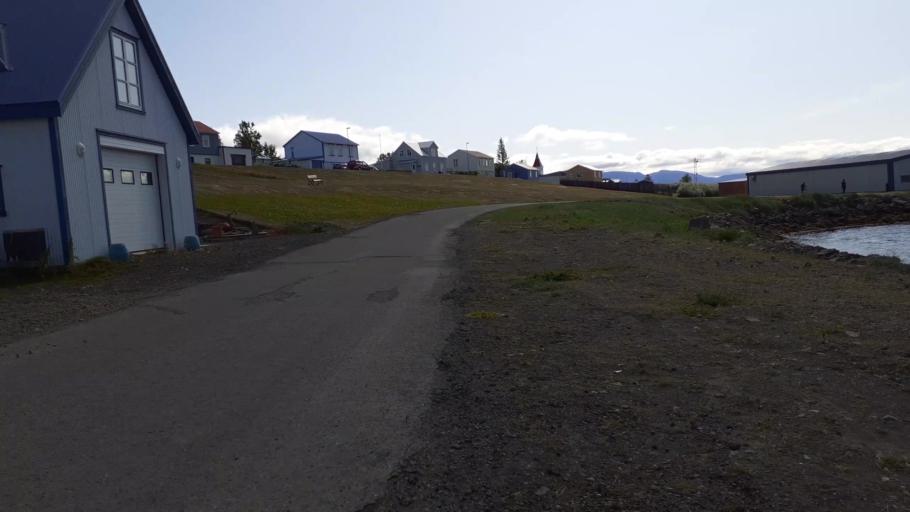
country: IS
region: Northeast
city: Dalvik
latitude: 65.9806
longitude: -18.3808
